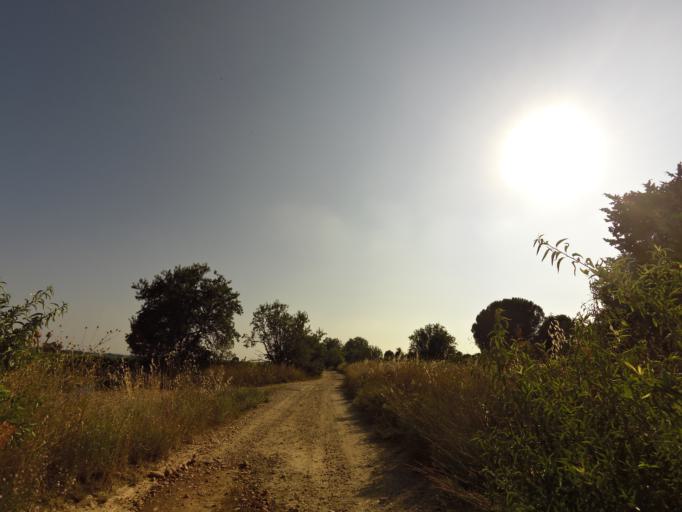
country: FR
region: Languedoc-Roussillon
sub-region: Departement du Gard
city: Mus
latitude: 43.7336
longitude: 4.2080
